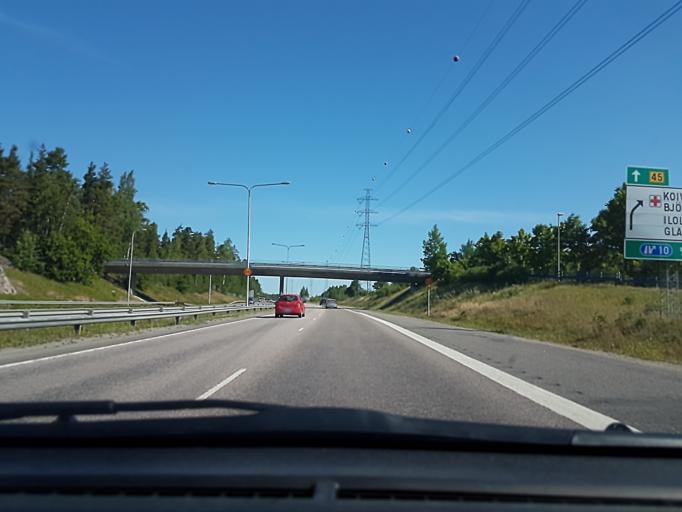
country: FI
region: Uusimaa
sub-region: Helsinki
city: Vantaa
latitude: 60.3108
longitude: 24.9981
